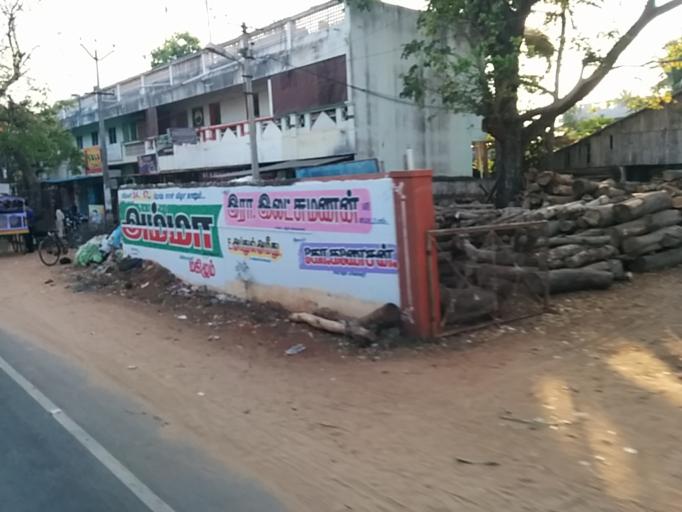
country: IN
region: Tamil Nadu
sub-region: Villupuram
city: Auroville
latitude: 11.9855
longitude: 79.8462
